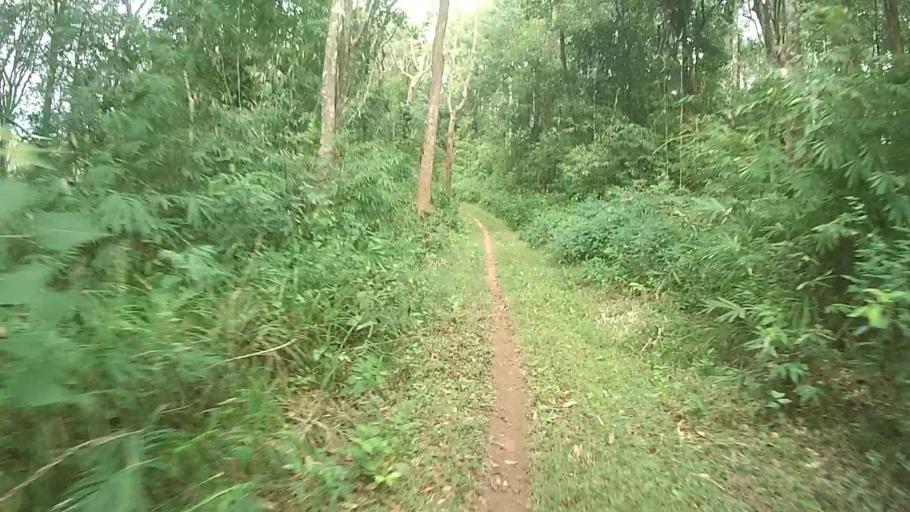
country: TH
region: Chiang Mai
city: Mae On
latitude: 18.8090
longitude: 99.3754
